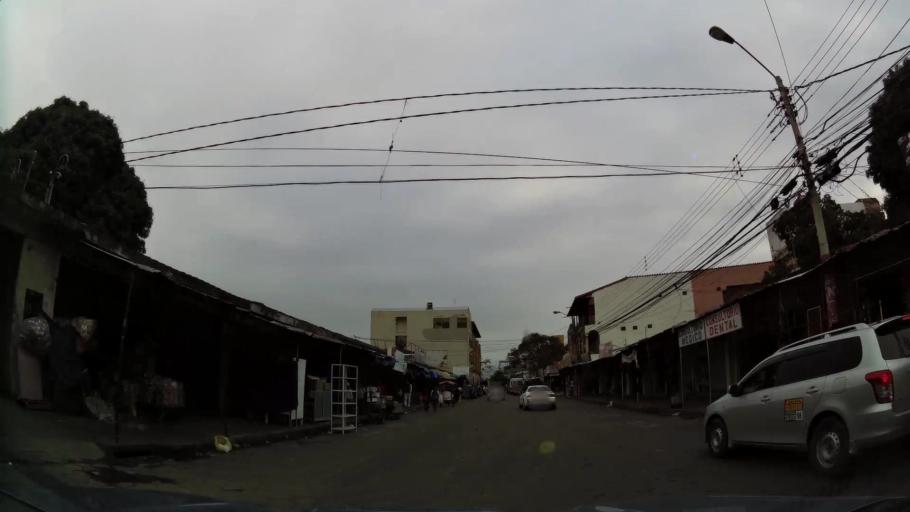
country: BO
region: Santa Cruz
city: Santa Cruz de la Sierra
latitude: -17.7939
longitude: -63.1916
